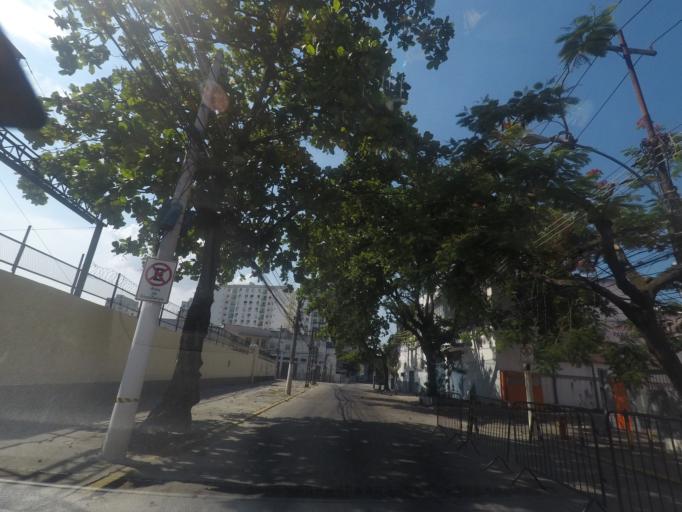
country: BR
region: Rio de Janeiro
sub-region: Rio De Janeiro
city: Rio de Janeiro
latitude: -22.8943
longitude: -43.2183
